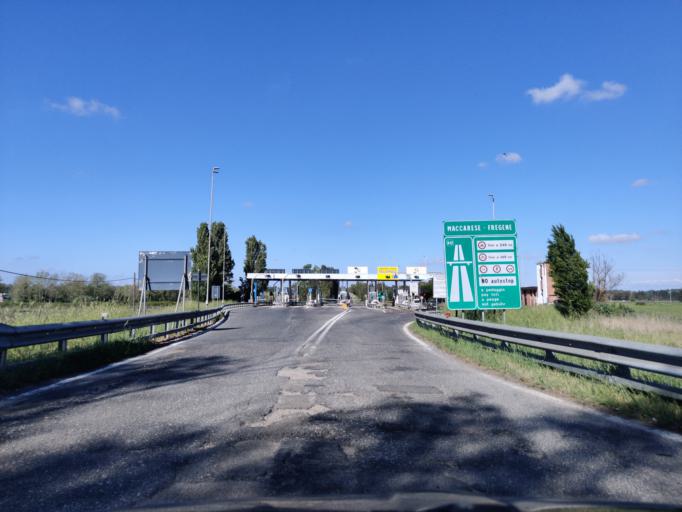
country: IT
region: Latium
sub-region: Citta metropolitana di Roma Capitale
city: Maccarese
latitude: 41.8852
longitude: 12.2230
